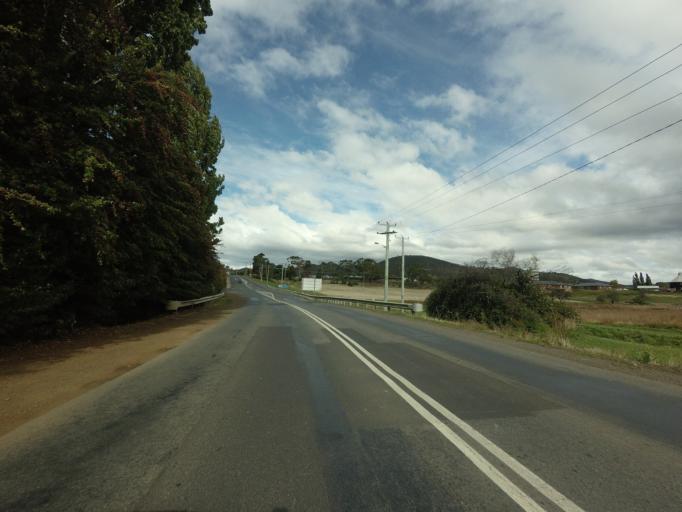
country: AU
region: Tasmania
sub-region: Derwent Valley
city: New Norfolk
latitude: -42.7786
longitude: 147.0712
